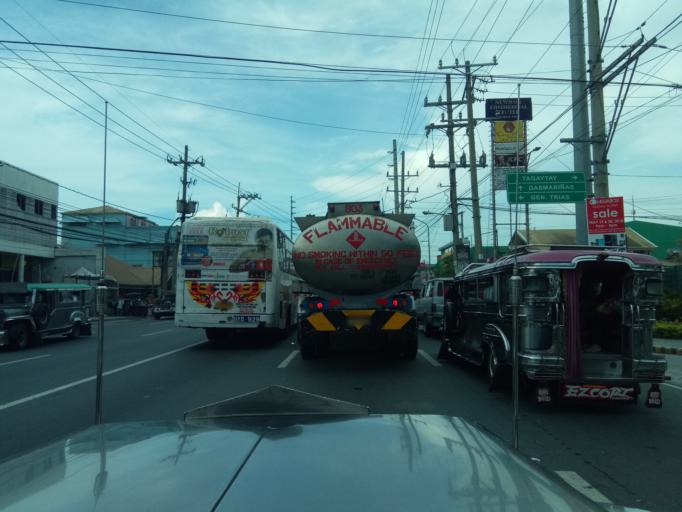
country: PH
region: Calabarzon
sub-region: Province of Cavite
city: Manggahan
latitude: 14.2919
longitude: 120.9095
